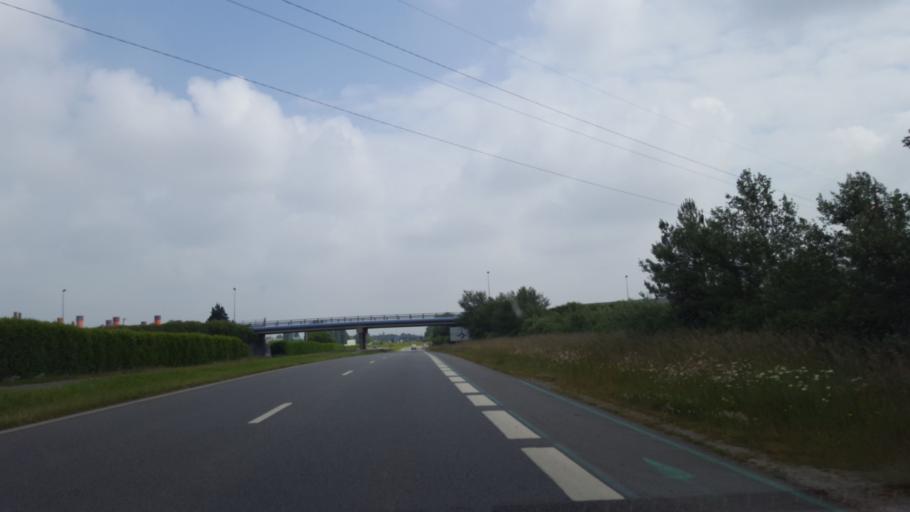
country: FR
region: Brittany
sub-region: Departement d'Ille-et-Vilaine
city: Chartres-de-Bretagne
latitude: 48.0528
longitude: -1.7055
